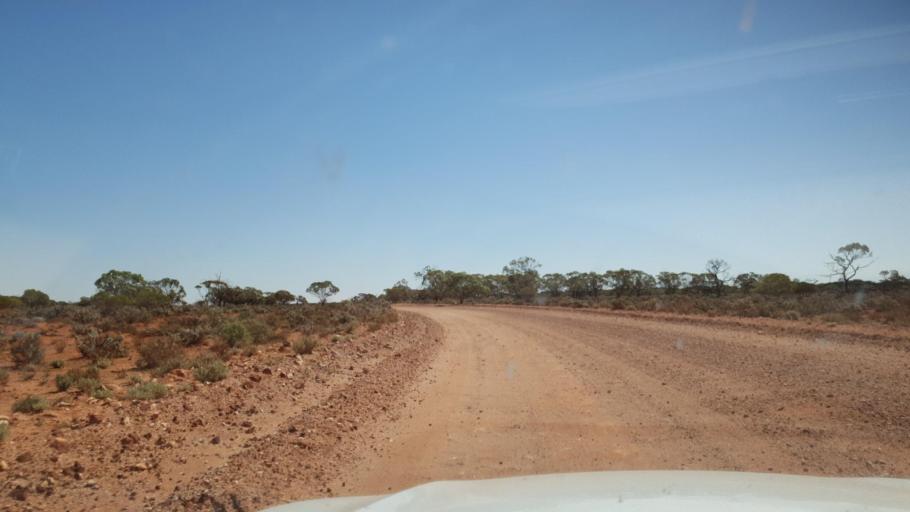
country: AU
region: South Australia
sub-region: Whyalla
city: Whyalla
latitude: -32.6511
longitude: 137.0204
